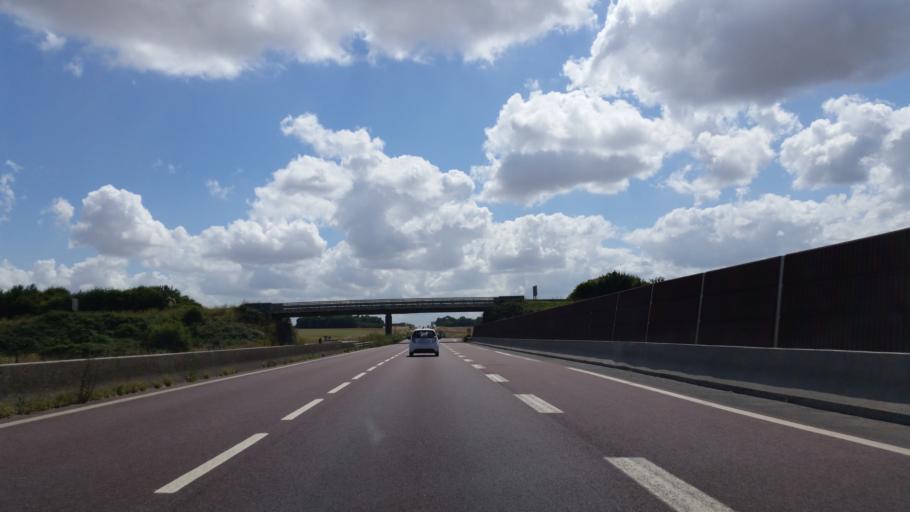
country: FR
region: Lower Normandy
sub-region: Departement du Calvados
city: Bourguebus
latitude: 49.0904
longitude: -0.3069
